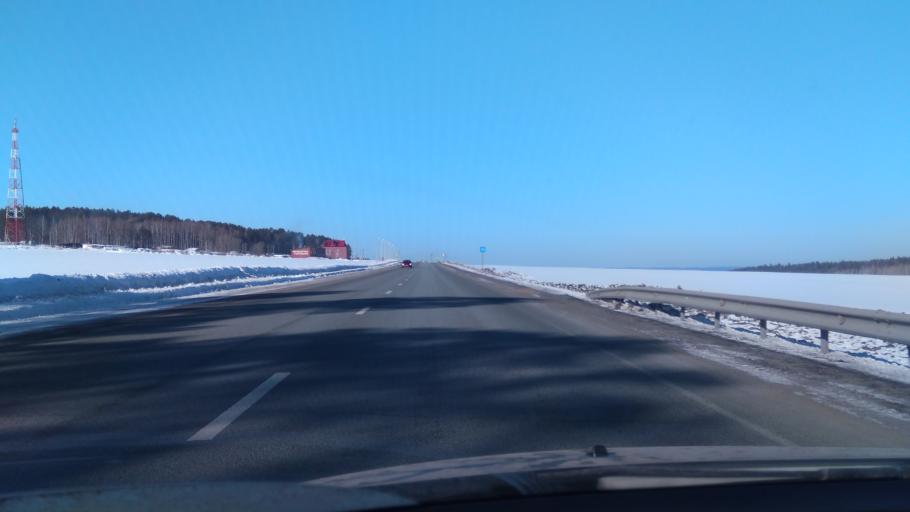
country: RU
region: Sverdlovsk
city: Bisert'
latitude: 56.8325
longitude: 58.8087
